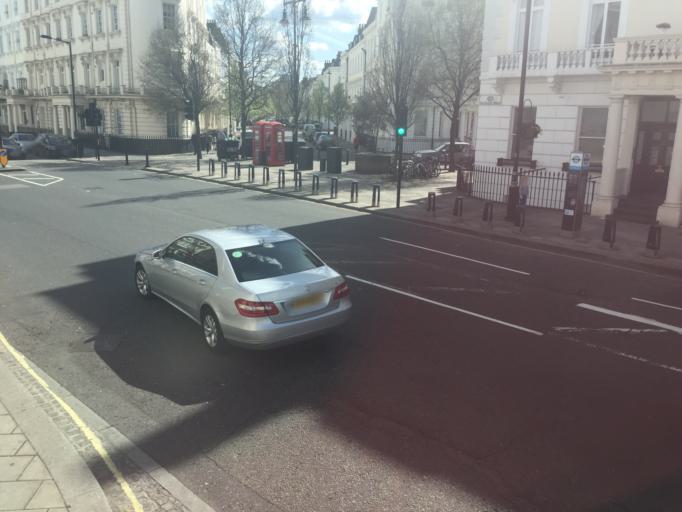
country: GB
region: England
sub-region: Greater London
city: London
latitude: 51.4912
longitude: -0.1397
